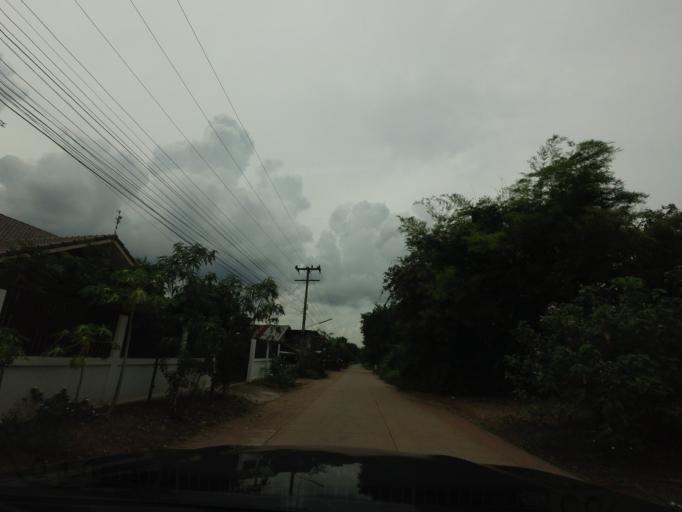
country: TH
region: Changwat Nong Bua Lamphu
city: Nong Bua Lamphu
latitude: 17.2715
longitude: 102.3924
